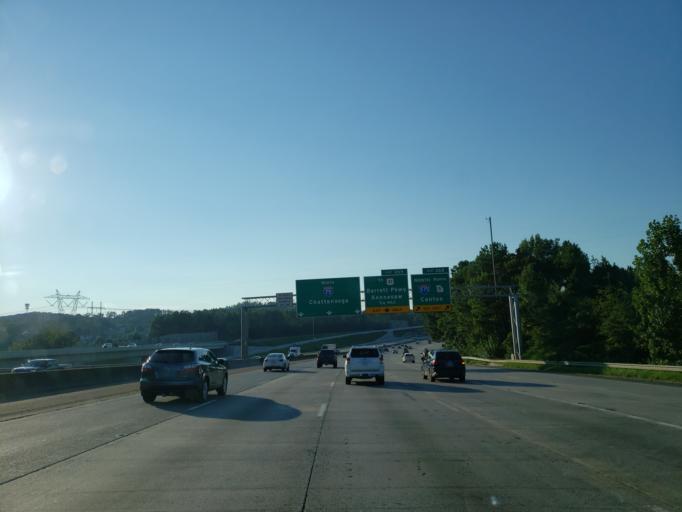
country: US
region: Georgia
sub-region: Cobb County
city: Marietta
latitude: 33.9966
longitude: -84.5590
